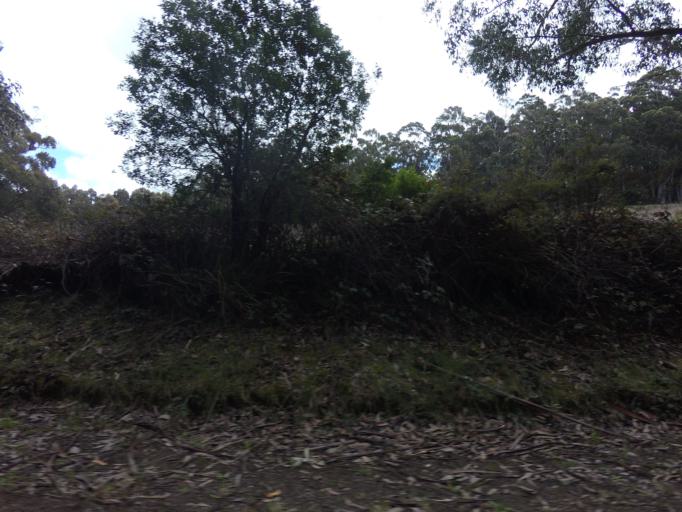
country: AU
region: Tasmania
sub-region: Huon Valley
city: Geeveston
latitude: -43.4166
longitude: 147.0149
